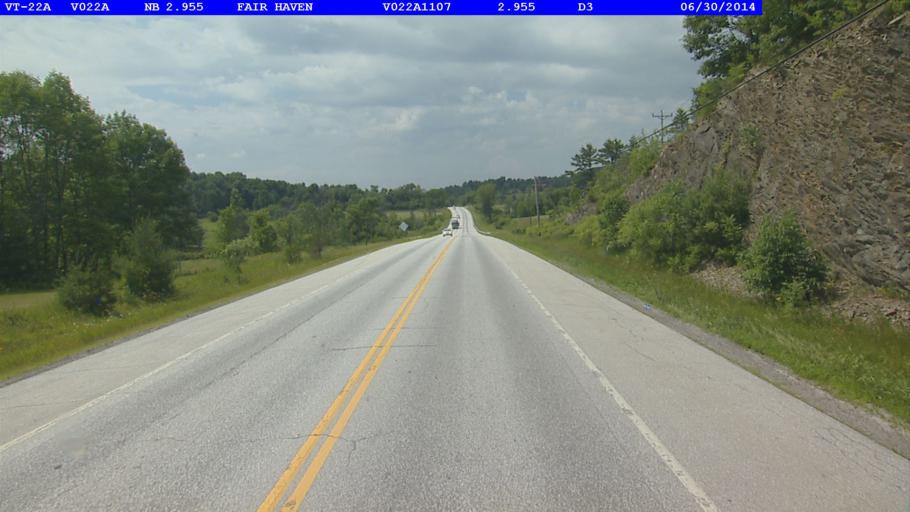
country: US
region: Vermont
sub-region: Rutland County
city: Fair Haven
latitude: 43.6105
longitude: -73.2835
